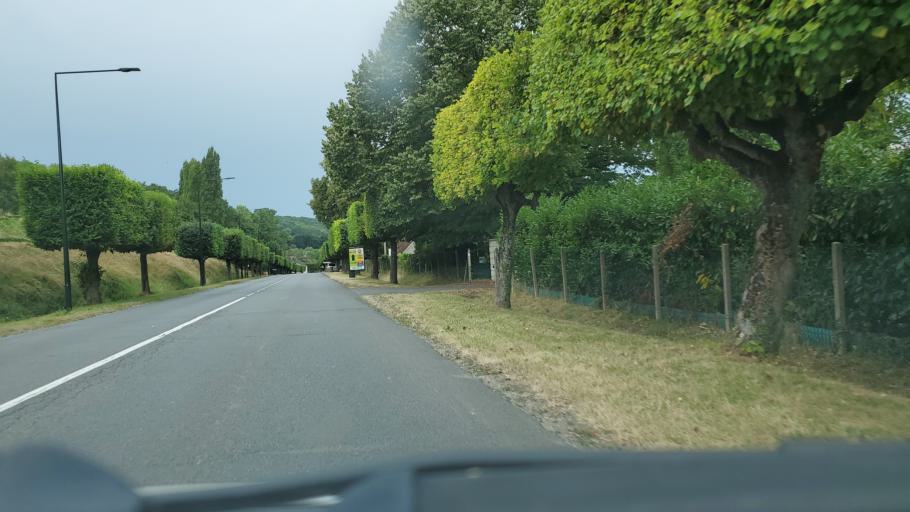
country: FR
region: Ile-de-France
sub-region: Departement de Seine-et-Marne
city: Coulommiers
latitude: 48.7988
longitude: 3.0917
